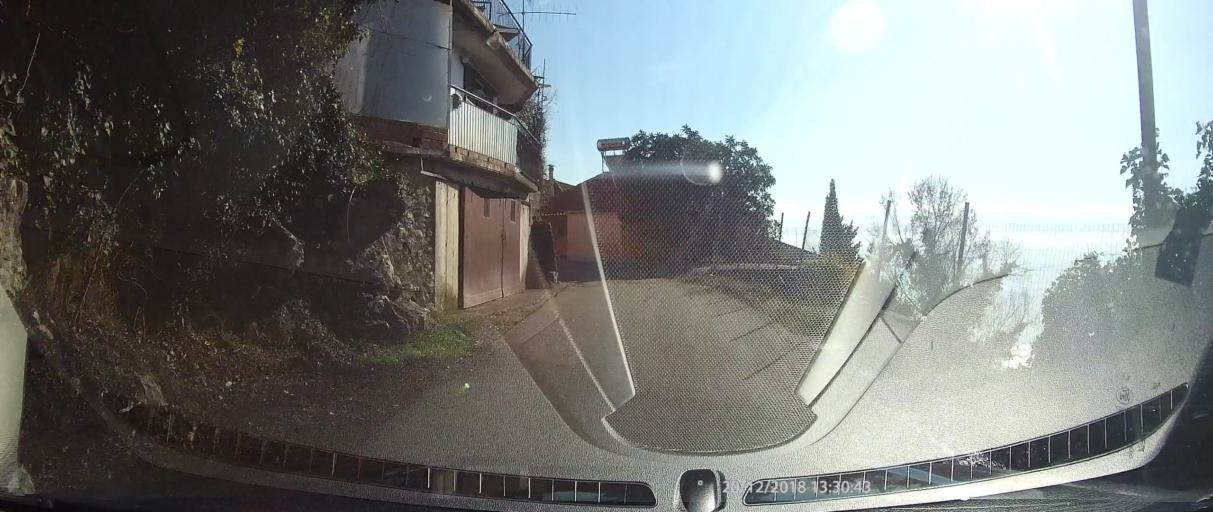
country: GR
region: West Greece
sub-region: Nomos Aitolias kai Akarnanias
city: Paravola
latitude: 38.6326
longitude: 21.5841
